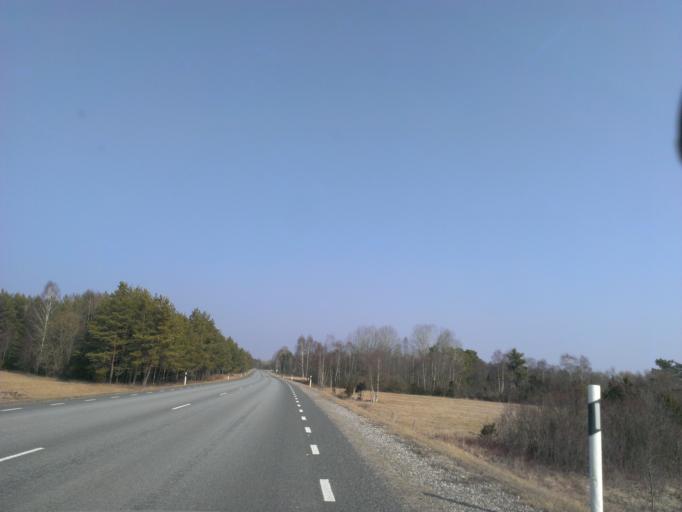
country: EE
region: Saare
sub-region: Orissaare vald
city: Orissaare
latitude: 58.5241
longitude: 22.9078
